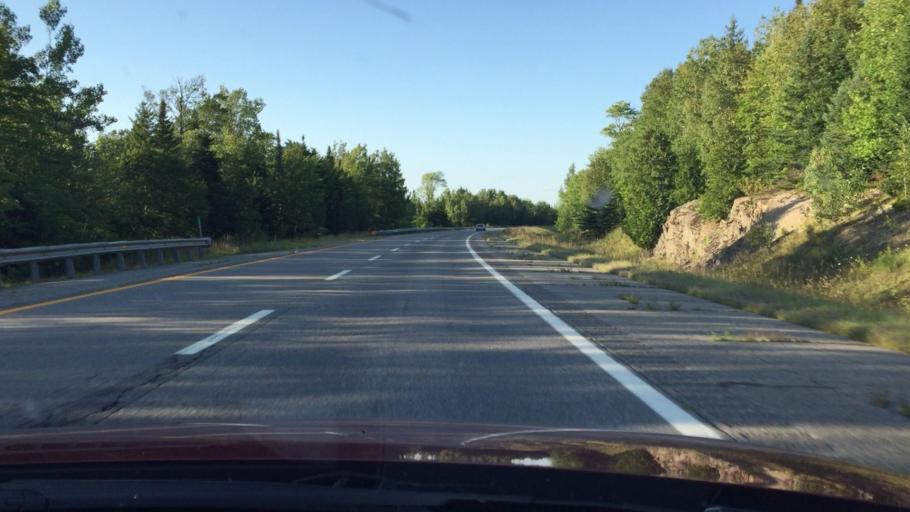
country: US
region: Maine
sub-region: Penobscot County
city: Patten
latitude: 45.8390
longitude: -68.4331
